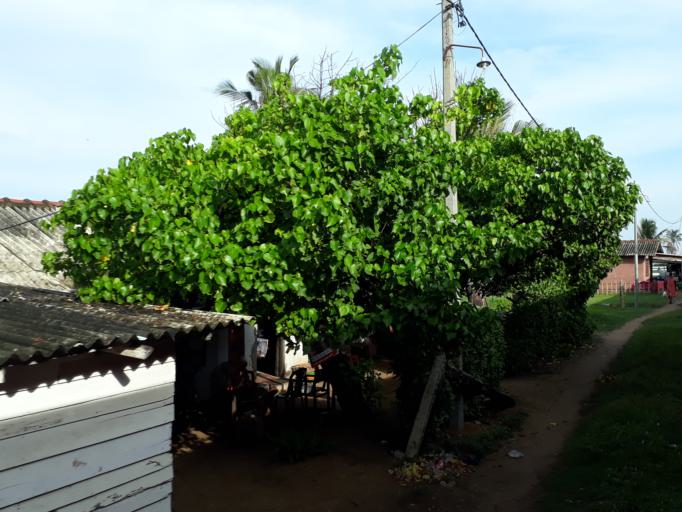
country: LK
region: Western
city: Moratuwa
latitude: 6.7876
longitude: 79.8753
